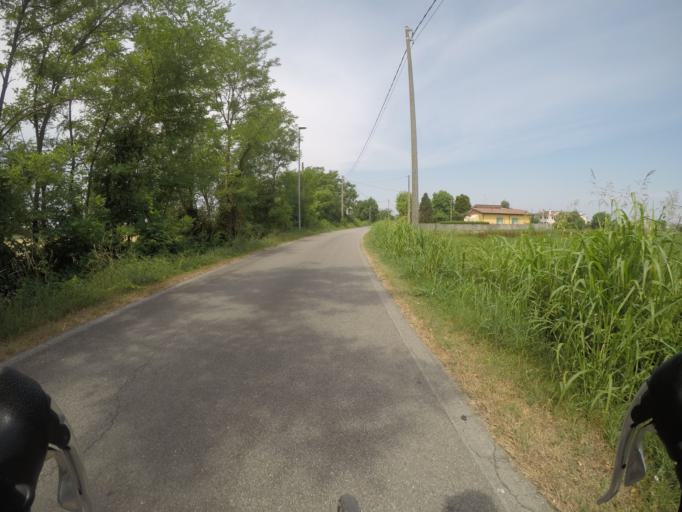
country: IT
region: Veneto
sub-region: Provincia di Rovigo
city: Villanova del Ghebbo Canton
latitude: 45.0499
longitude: 11.6538
